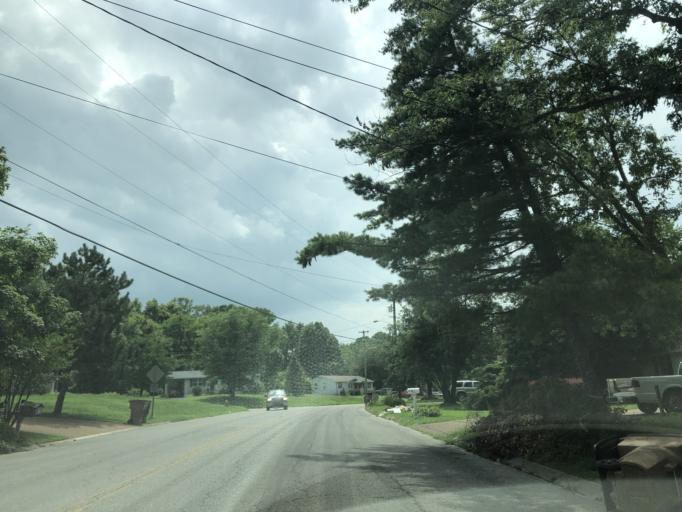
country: US
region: Tennessee
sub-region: Williamson County
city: Brentwood Estates
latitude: 36.0569
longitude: -86.6796
